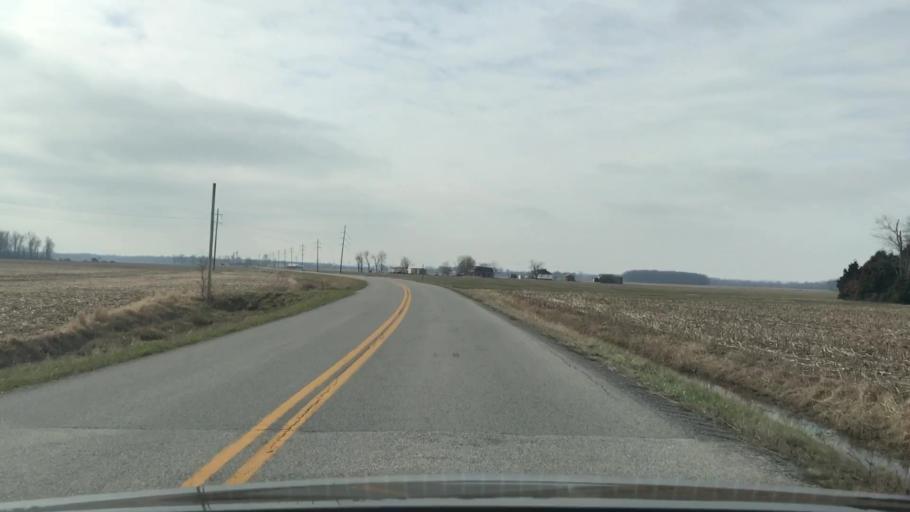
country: US
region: Kentucky
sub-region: McLean County
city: Calhoun
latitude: 37.5339
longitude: -87.3180
